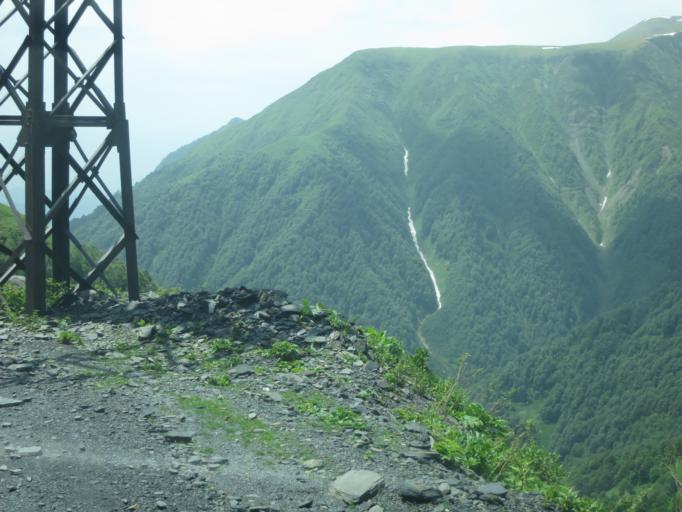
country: GE
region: Kakheti
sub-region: Telavi
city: Telavi
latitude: 42.2665
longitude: 45.5046
